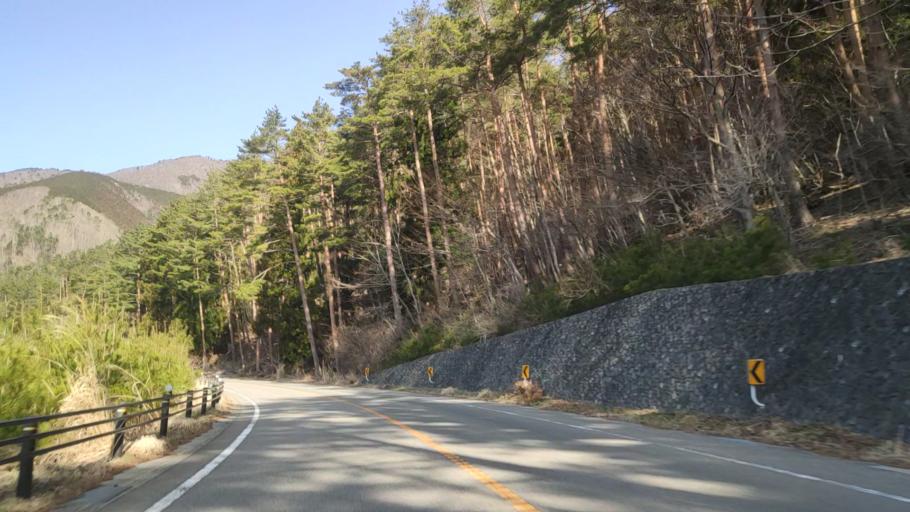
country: JP
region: Yamanashi
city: Fujikawaguchiko
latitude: 35.5274
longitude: 138.7180
